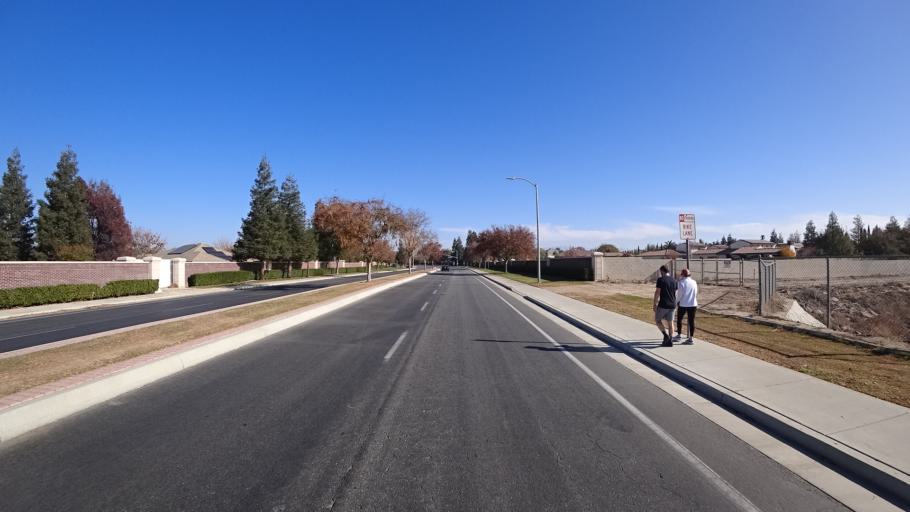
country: US
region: California
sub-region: Kern County
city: Rosedale
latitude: 35.3575
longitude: -119.1324
